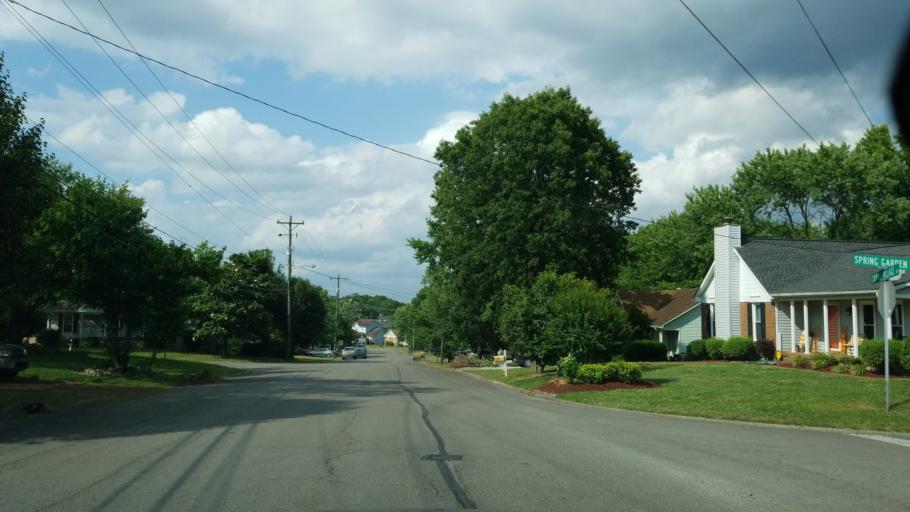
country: US
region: Tennessee
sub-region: Rutherford County
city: La Vergne
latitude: 36.0704
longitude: -86.6023
